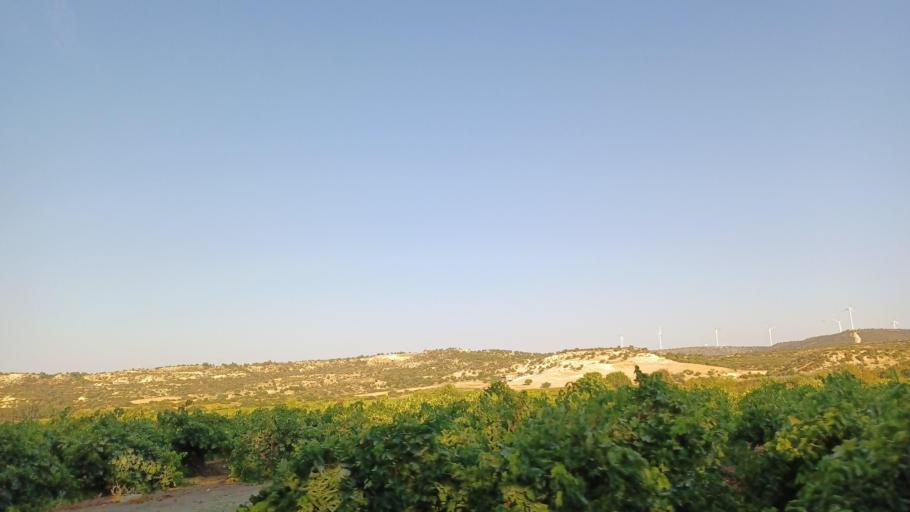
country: CY
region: Limassol
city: Pissouri
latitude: 34.7035
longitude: 32.6760
